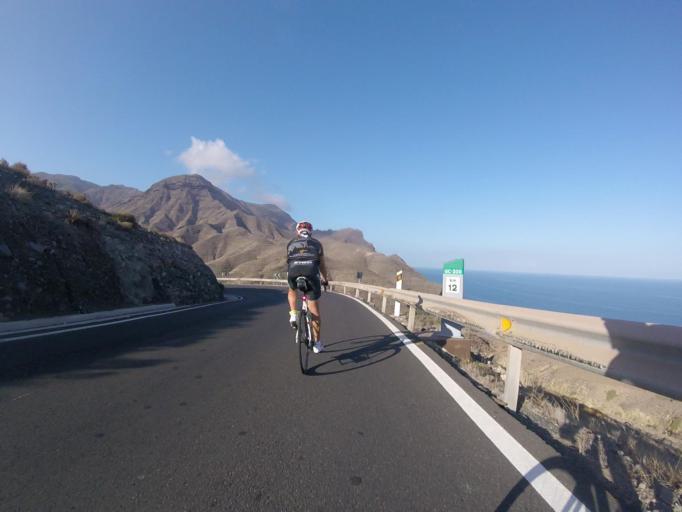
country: ES
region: Canary Islands
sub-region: Provincia de Las Palmas
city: Agaete
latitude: 28.0539
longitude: -15.7332
